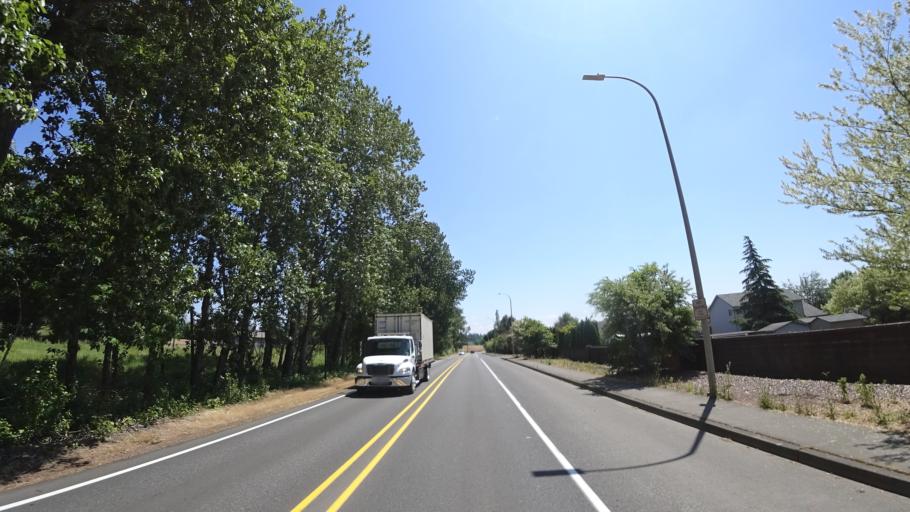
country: US
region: Oregon
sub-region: Multnomah County
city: Fairview
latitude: 45.5535
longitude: -122.4346
